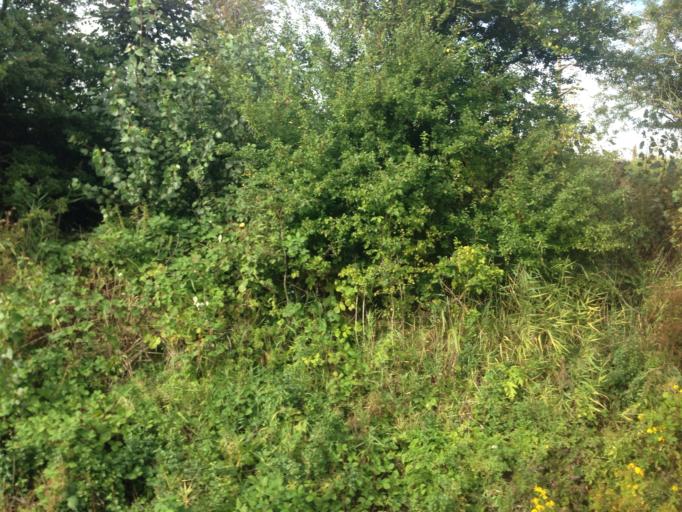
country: DE
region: Schleswig-Holstein
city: Sylt-Ost
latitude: 54.8718
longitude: 8.4408
